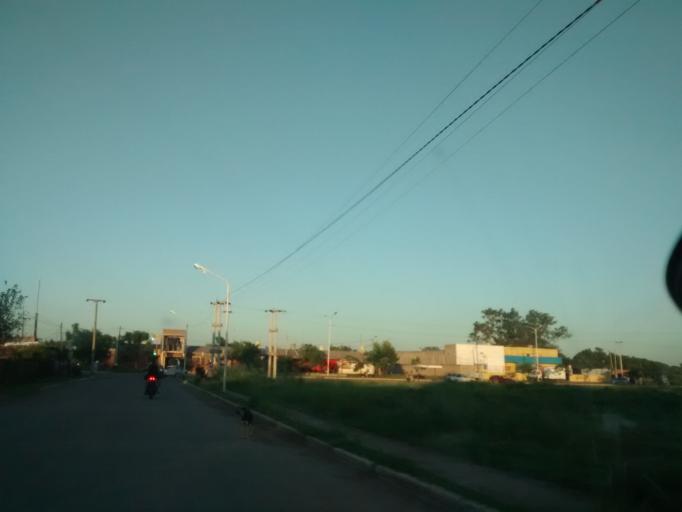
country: AR
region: Chaco
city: Fontana
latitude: -27.4139
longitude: -59.0299
